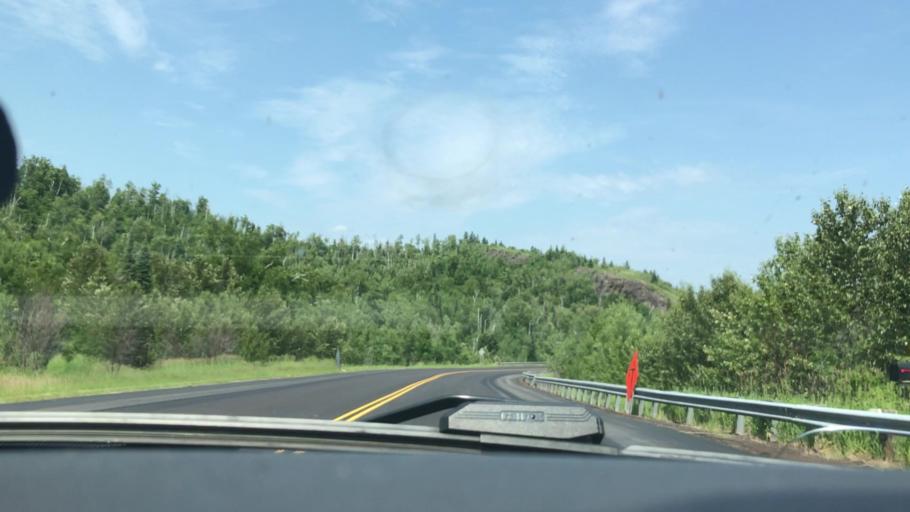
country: US
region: Minnesota
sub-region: Lake County
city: Silver Bay
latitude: 47.3748
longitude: -91.1640
